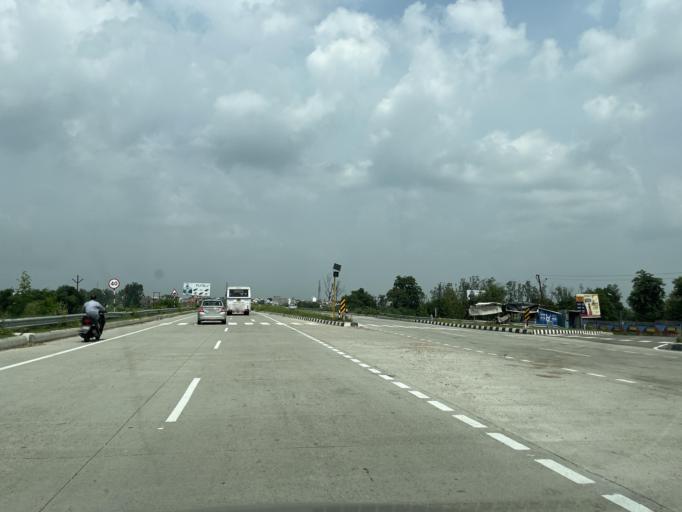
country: IN
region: Uttar Pradesh
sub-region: Bijnor
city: Sherkot
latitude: 29.3241
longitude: 78.5636
